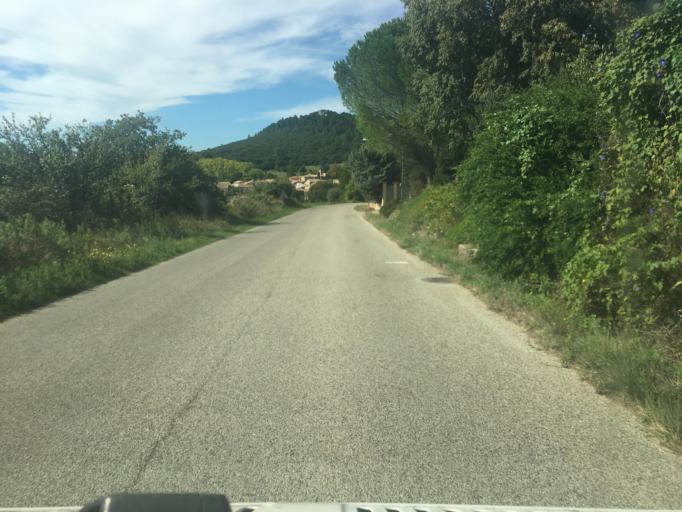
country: FR
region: Languedoc-Roussillon
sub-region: Departement du Gard
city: Saint-Quentin-la-Poterie
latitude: 44.0306
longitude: 4.4949
